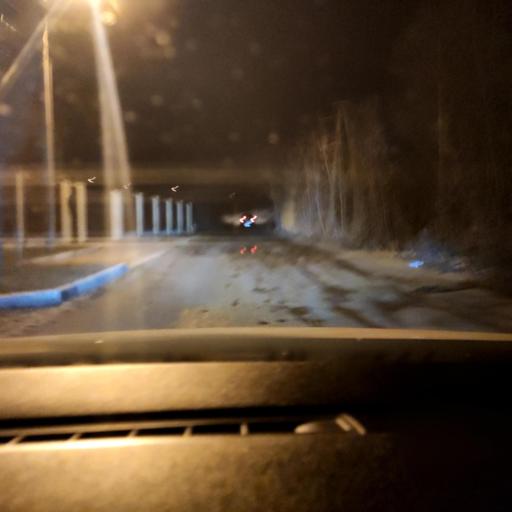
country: RU
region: Voronezj
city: Pridonskoy
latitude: 51.6860
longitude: 39.0599
